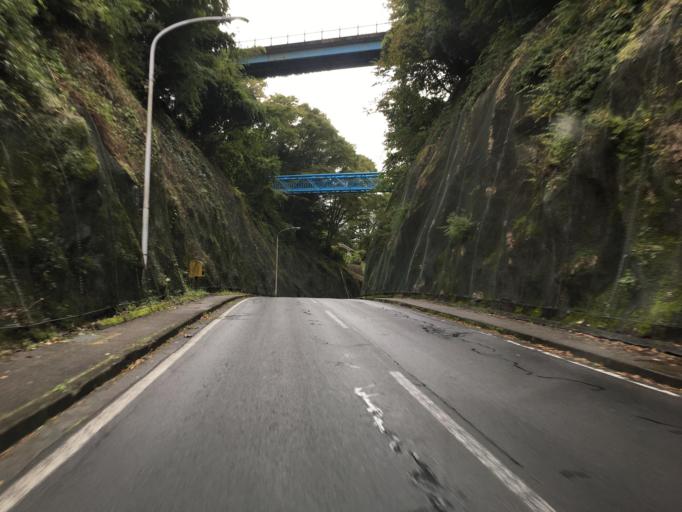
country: JP
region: Fukushima
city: Nihommatsu
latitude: 37.5959
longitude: 140.4403
